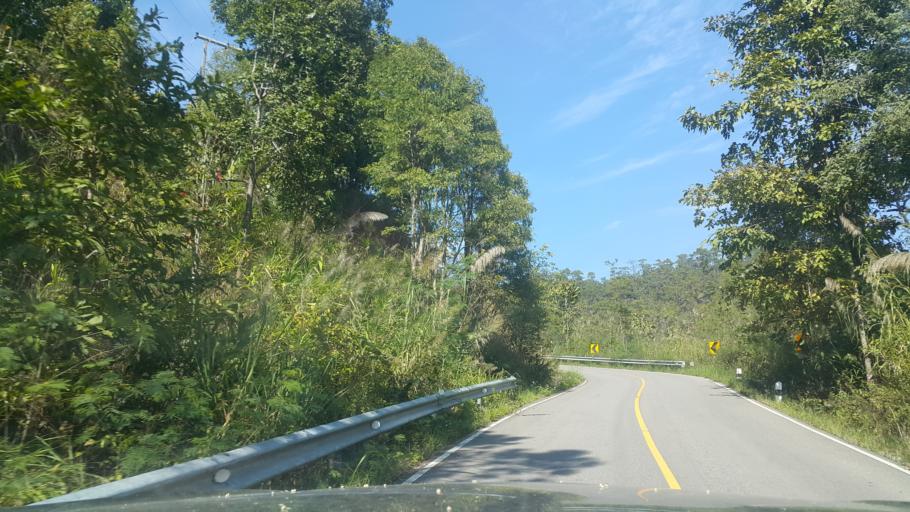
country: TH
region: Chiang Mai
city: Samoeng
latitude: 18.9036
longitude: 98.6764
